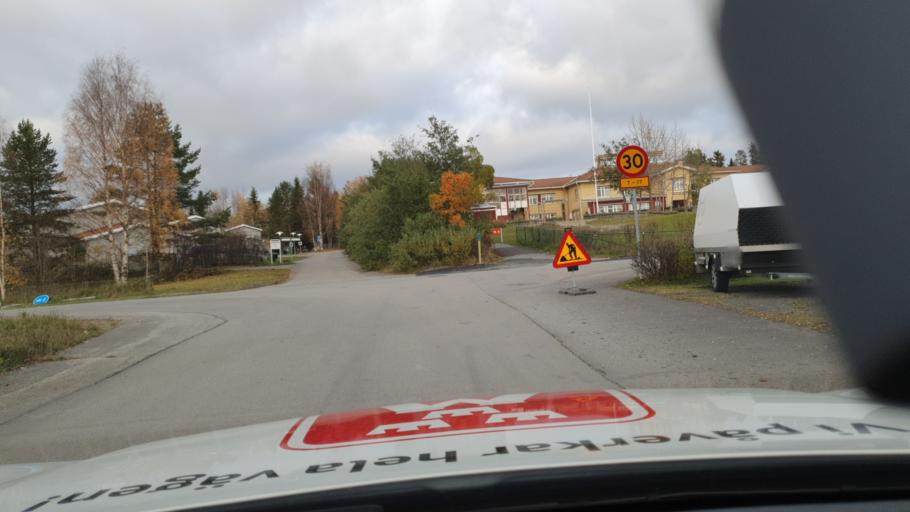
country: SE
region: Jaemtland
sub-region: OEstersunds Kommun
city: Ostersund
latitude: 63.1549
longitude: 14.7469
